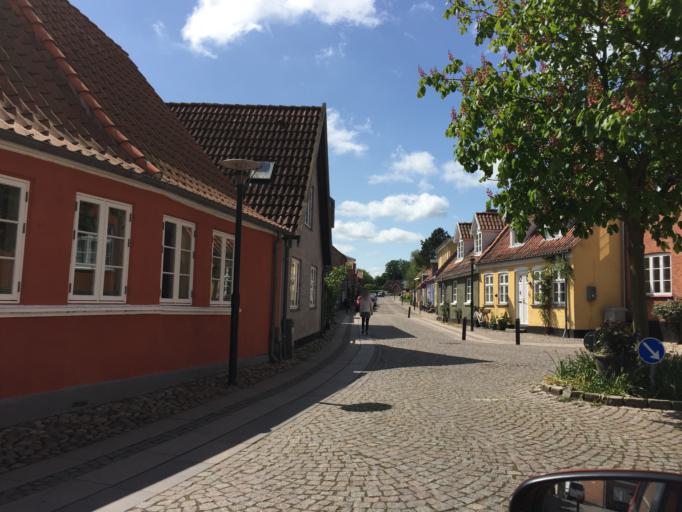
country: DK
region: South Denmark
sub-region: Middelfart Kommune
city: Middelfart
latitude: 55.5055
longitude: 9.7256
